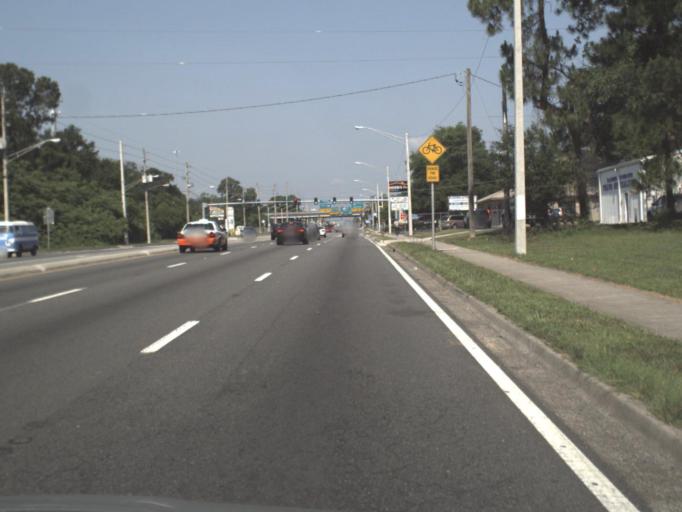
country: US
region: Florida
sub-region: Clay County
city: Bellair-Meadowbrook Terrace
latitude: 30.2485
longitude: -81.7581
